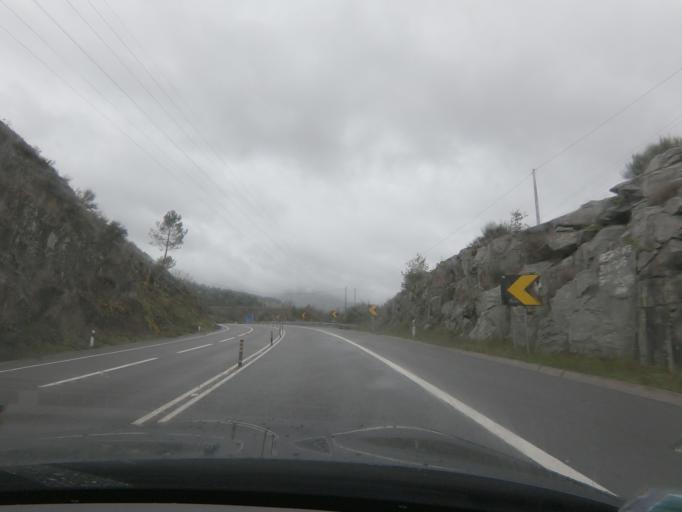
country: PT
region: Vila Real
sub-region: Santa Marta de Penaguiao
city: Santa Marta de Penaguiao
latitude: 41.2849
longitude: -7.8308
